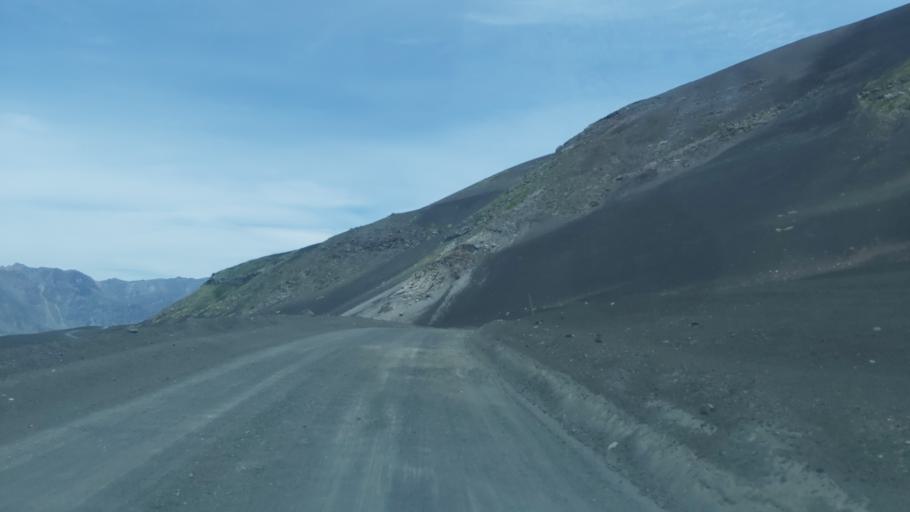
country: AR
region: Neuquen
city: Andacollo
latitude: -37.4017
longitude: -71.3021
